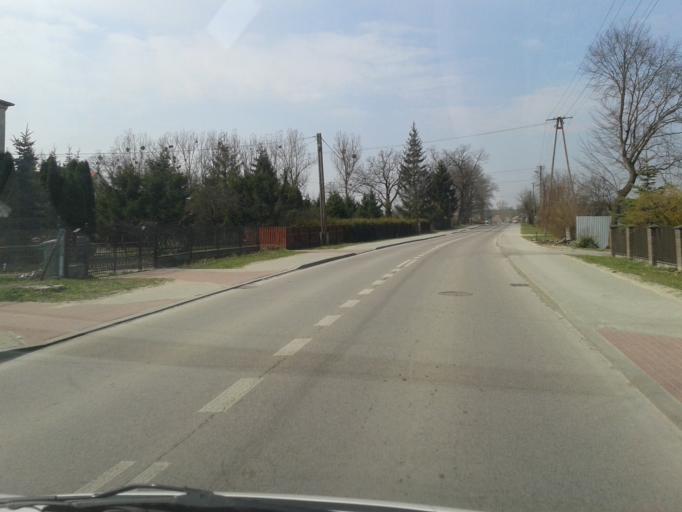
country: PL
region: Lublin Voivodeship
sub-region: Powiat tomaszowski
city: Belzec
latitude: 50.3833
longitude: 23.4235
